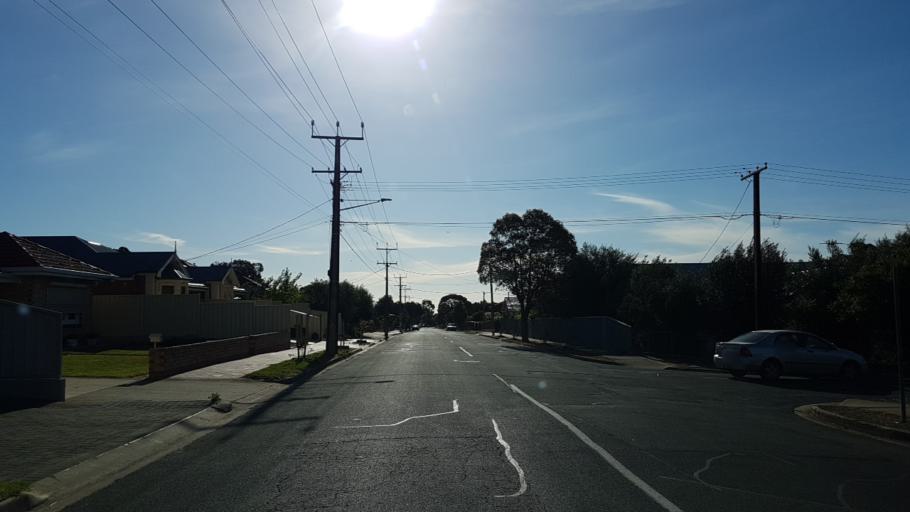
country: AU
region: South Australia
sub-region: Campbelltown
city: Campbelltown
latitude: -34.8945
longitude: 138.6796
